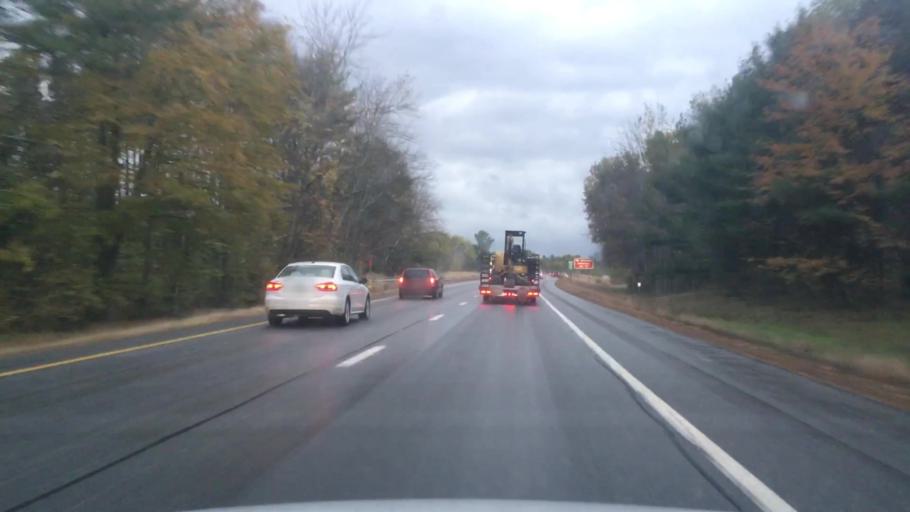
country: US
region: New Hampshire
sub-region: Merrimack County
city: East Concord
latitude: 43.2702
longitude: -71.5585
